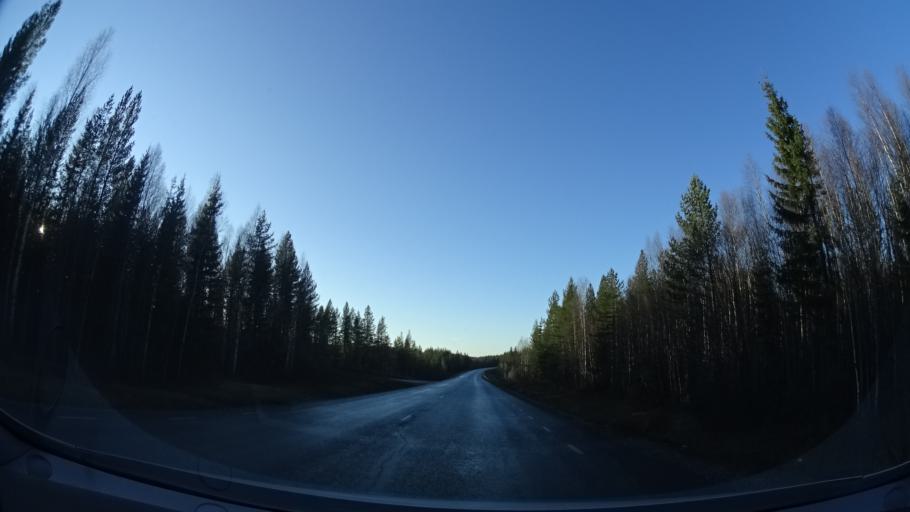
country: SE
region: Vaesterbotten
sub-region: Skelleftea Kommun
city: Langsele
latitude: 64.8842
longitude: 20.2165
